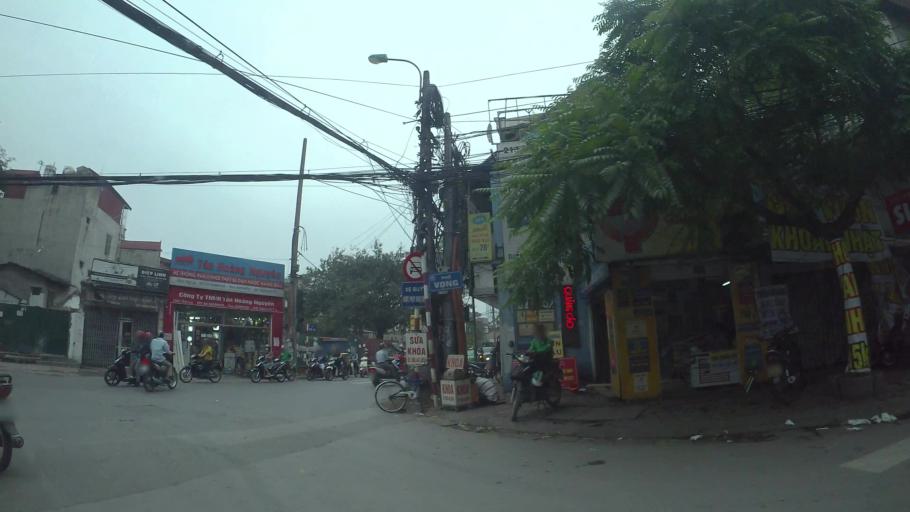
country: VN
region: Ha Noi
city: Hai BaTrung
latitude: 20.9972
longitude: 105.8428
